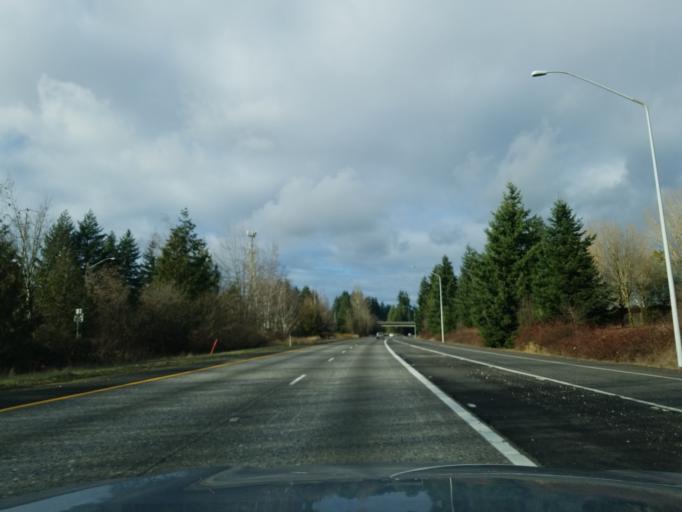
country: US
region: Washington
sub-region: Clark County
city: Barberton
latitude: 45.6852
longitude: -122.5976
